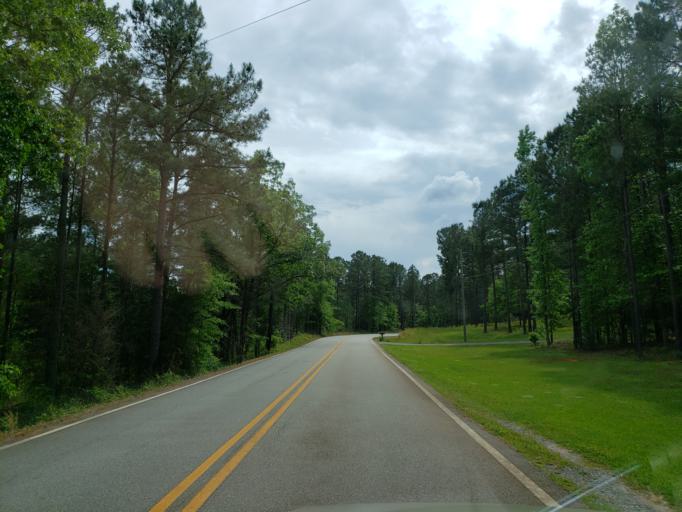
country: US
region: Georgia
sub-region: Monroe County
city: Forsyth
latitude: 32.9450
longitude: -83.9338
